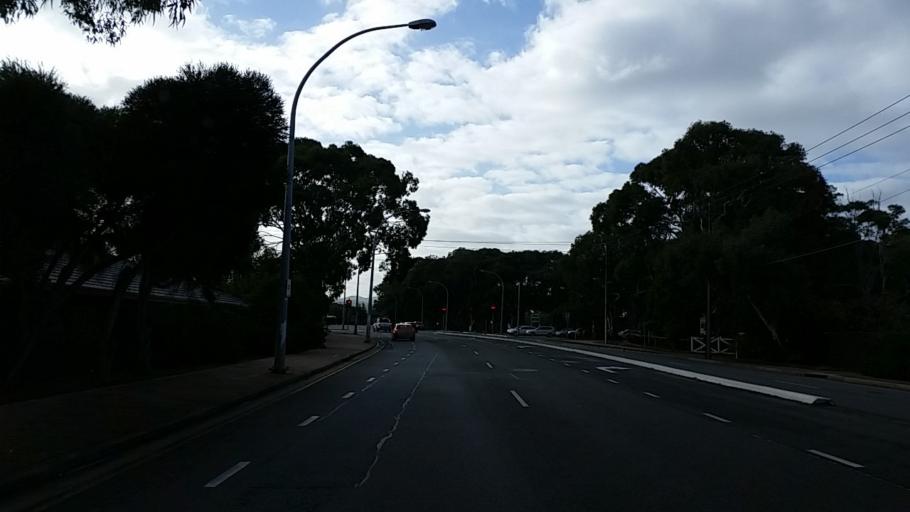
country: AU
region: South Australia
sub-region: Marion
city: Plympton Park
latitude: -34.9962
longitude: 138.5380
